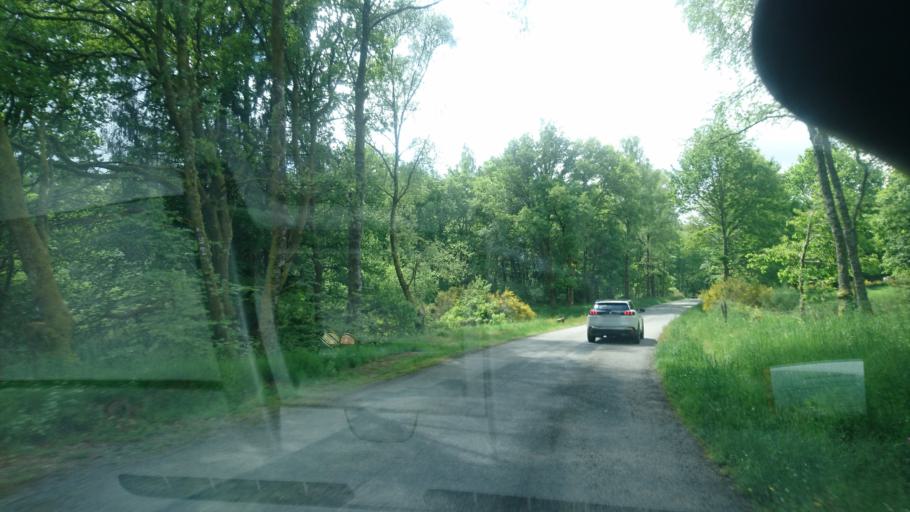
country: FR
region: Limousin
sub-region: Departement de la Haute-Vienne
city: Peyrat-le-Chateau
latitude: 45.7865
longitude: 1.9012
